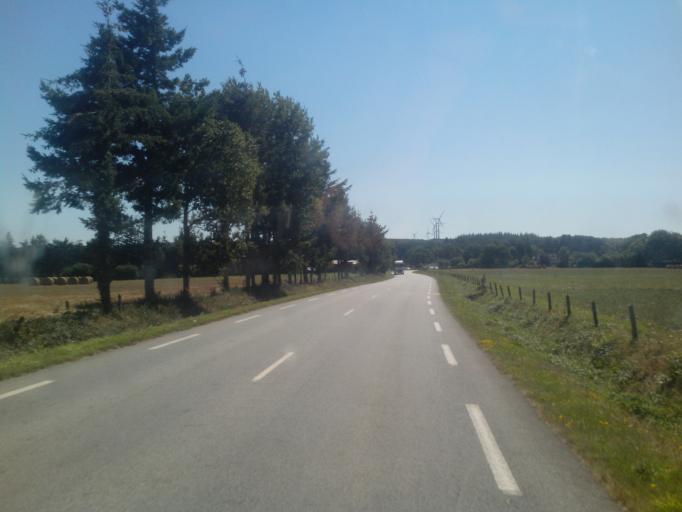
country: FR
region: Brittany
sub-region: Departement du Morbihan
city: Guegon
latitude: 47.9194
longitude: -2.5258
